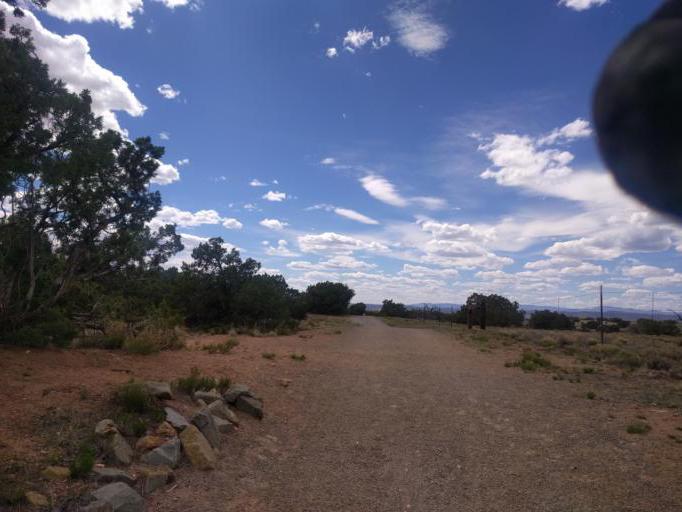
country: US
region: New Mexico
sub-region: Santa Fe County
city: Agua Fria
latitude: 35.5990
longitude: -105.9969
